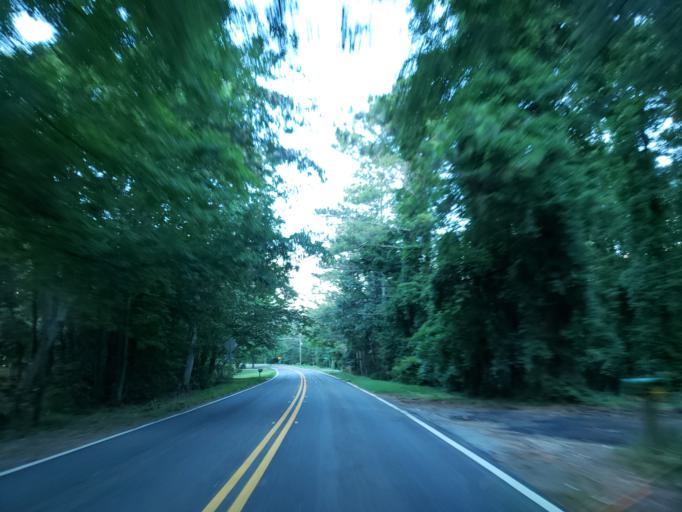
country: US
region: Georgia
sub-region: Bartow County
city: Emerson
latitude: 34.1873
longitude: -84.7378
